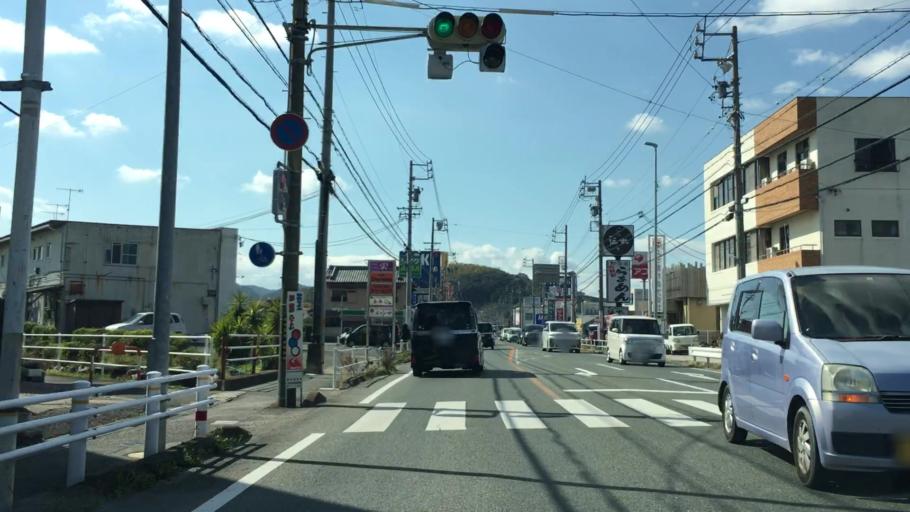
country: JP
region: Aichi
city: Gamagori
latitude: 34.8253
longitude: 137.2108
